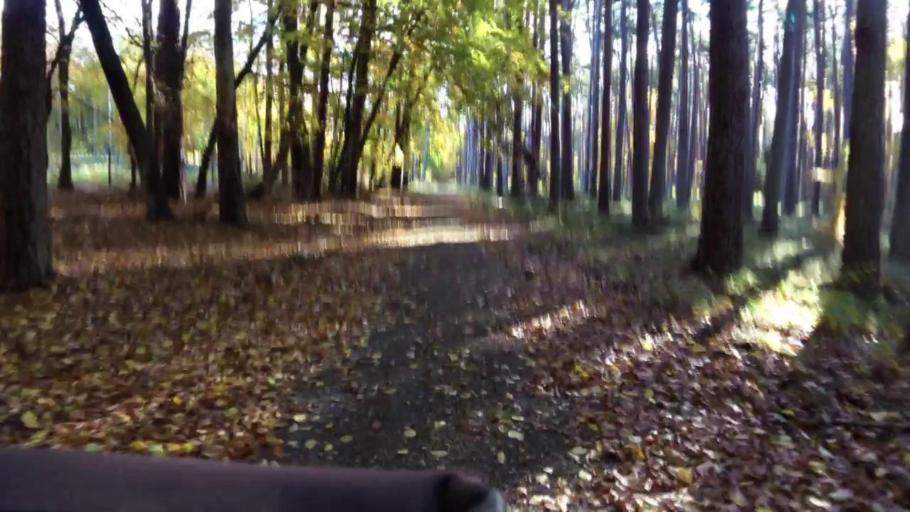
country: PL
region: West Pomeranian Voivodeship
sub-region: Powiat kamienski
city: Miedzyzdroje
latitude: 53.8672
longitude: 14.4952
